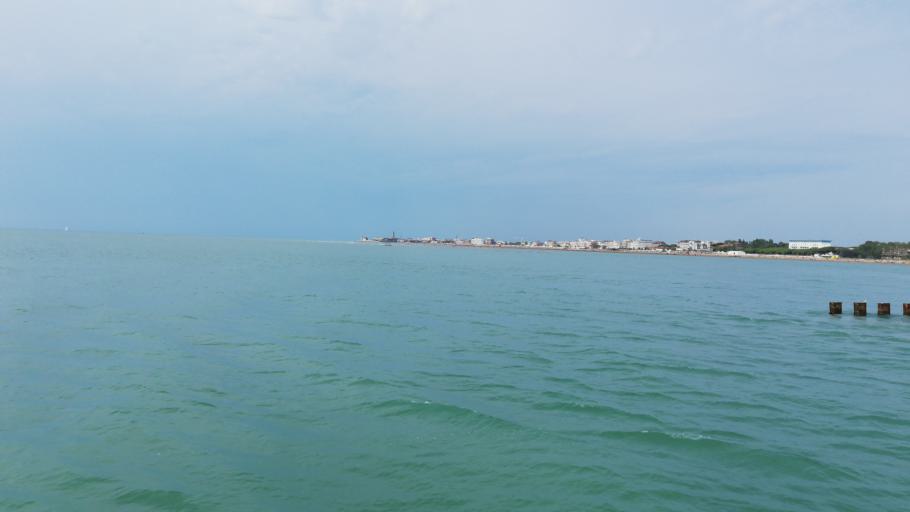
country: IT
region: Veneto
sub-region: Provincia di Venezia
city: Caorle
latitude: 45.6118
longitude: 12.9129
